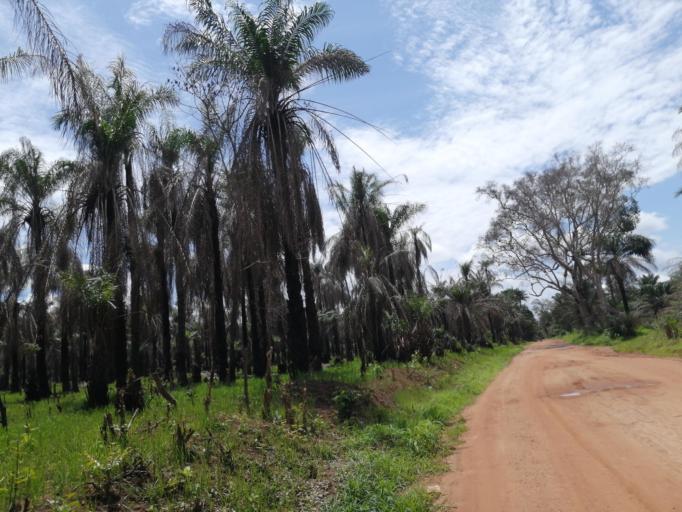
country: SL
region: Northern Province
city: Konakridee
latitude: 8.7438
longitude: -13.1459
